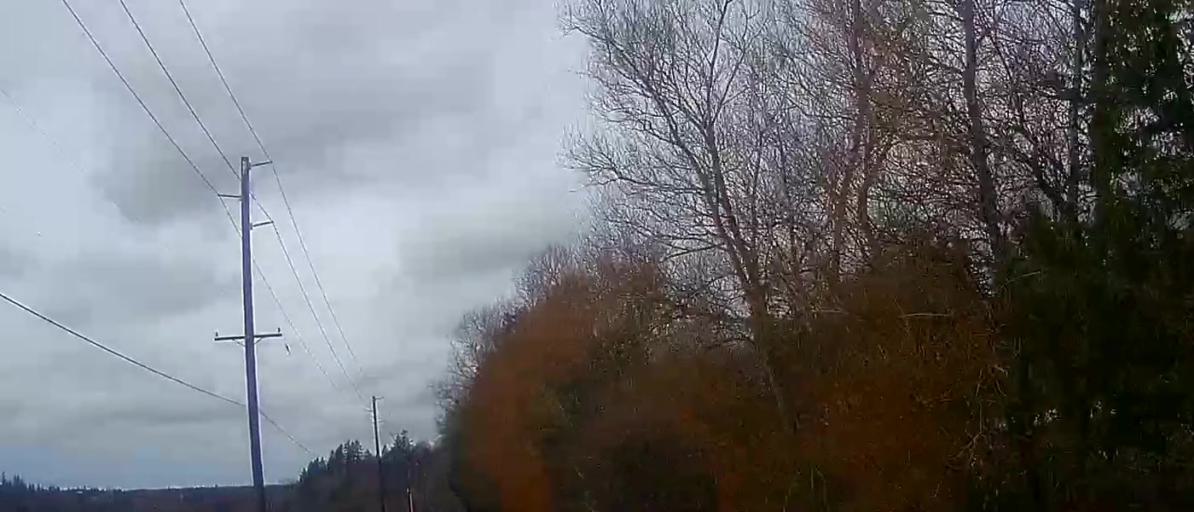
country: US
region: Washington
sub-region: Skagit County
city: Burlington
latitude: 48.5580
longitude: -122.3134
